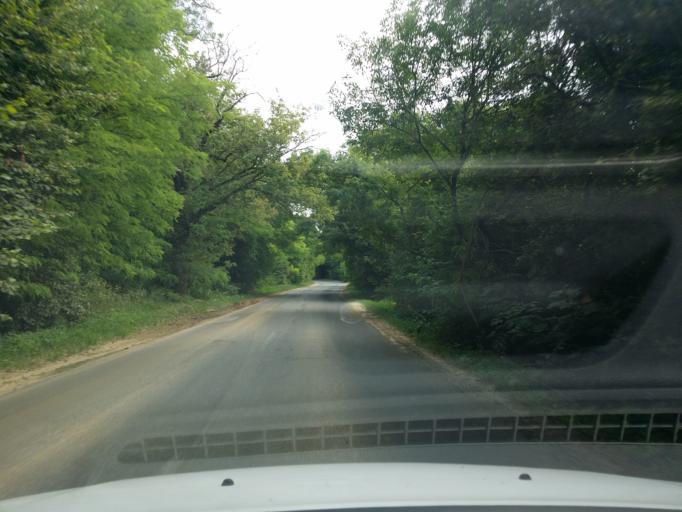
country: HU
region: Pest
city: Acsa
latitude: 47.8123
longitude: 19.3879
